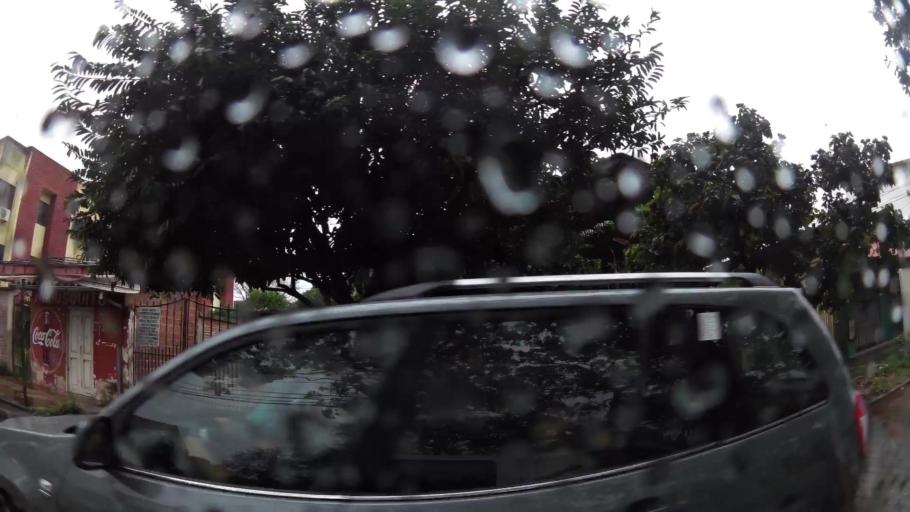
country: BO
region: Santa Cruz
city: Santa Cruz de la Sierra
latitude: -17.7891
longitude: -63.2097
